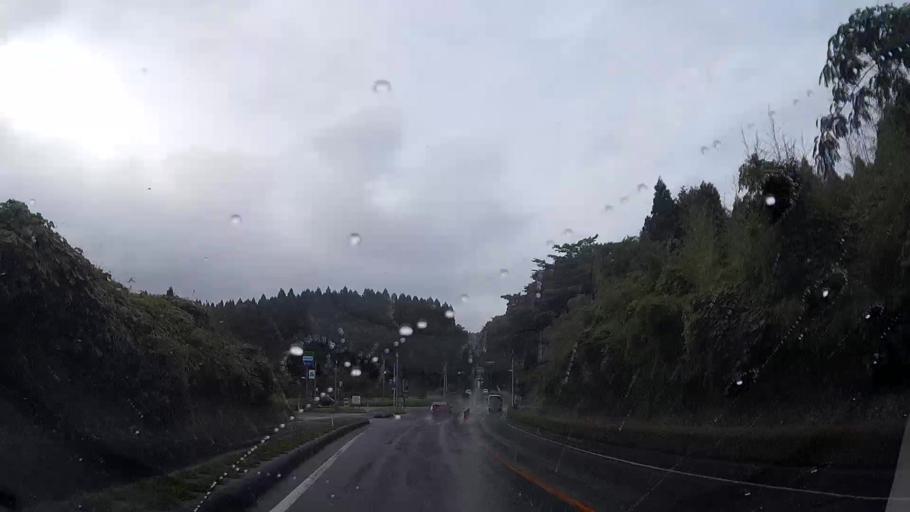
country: JP
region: Kumamoto
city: Aso
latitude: 32.8643
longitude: 131.0007
